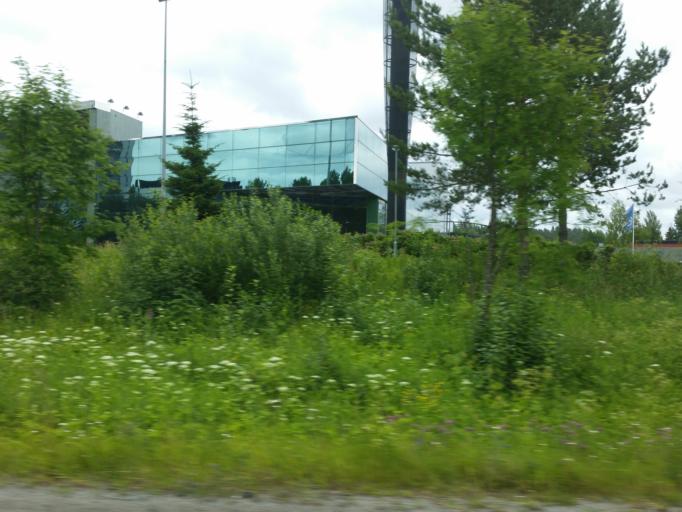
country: FI
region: Northern Savo
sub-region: Kuopio
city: Kuopio
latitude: 62.8859
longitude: 27.6291
